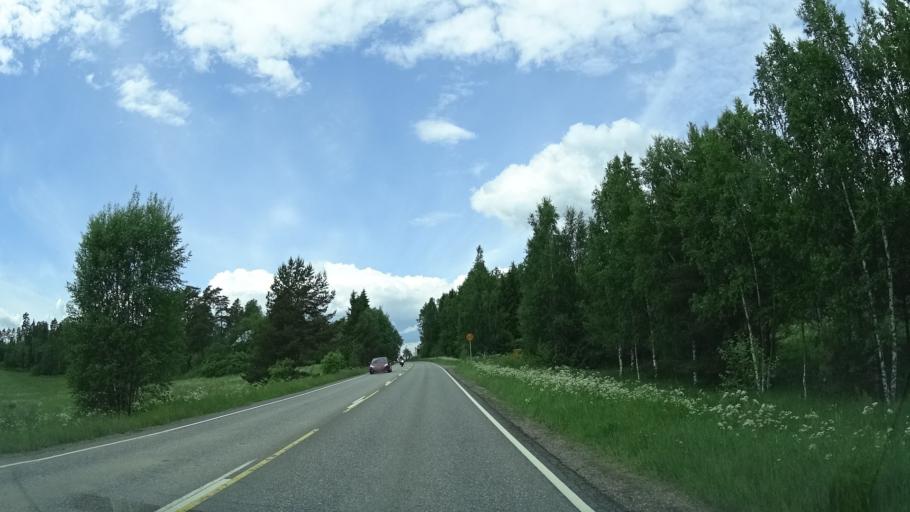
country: FI
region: Uusimaa
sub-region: Helsinki
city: Espoo
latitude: 60.1974
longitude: 24.5582
